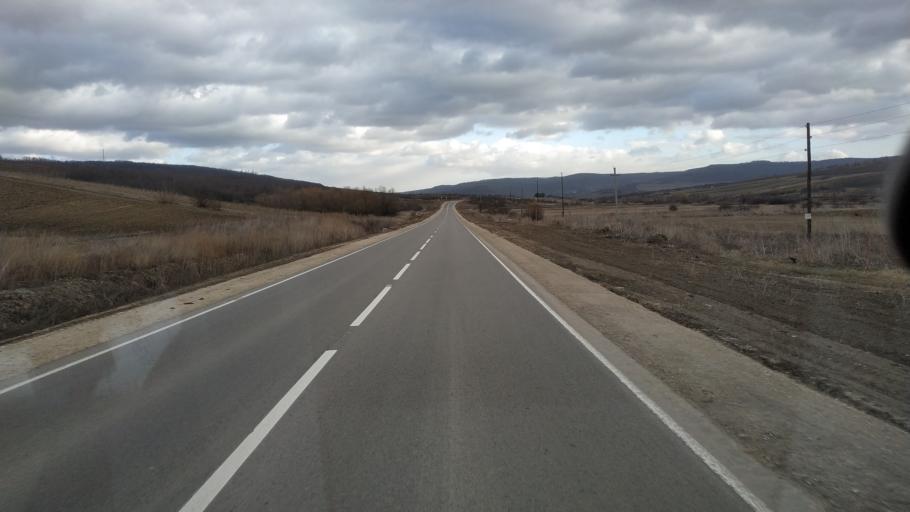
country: MD
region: Calarasi
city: Calarasi
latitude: 47.2735
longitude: 28.2202
